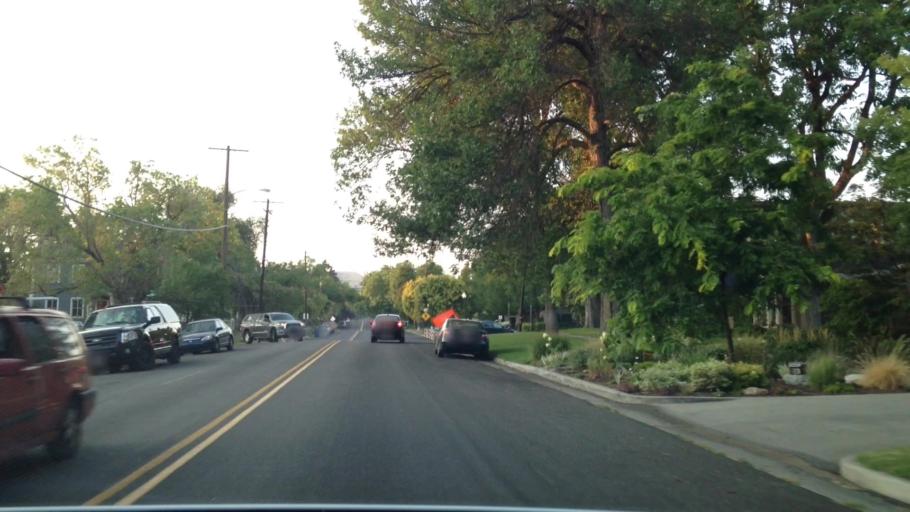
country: US
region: Utah
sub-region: Salt Lake County
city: Salt Lake City
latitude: 40.7744
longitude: -111.8775
